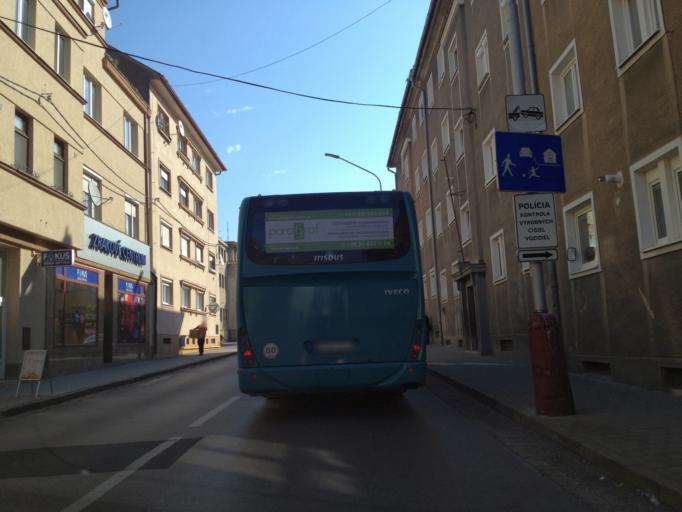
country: SK
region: Nitriansky
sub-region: Okres Nove Zamky
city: Nove Zamky
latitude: 47.9866
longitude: 18.1607
